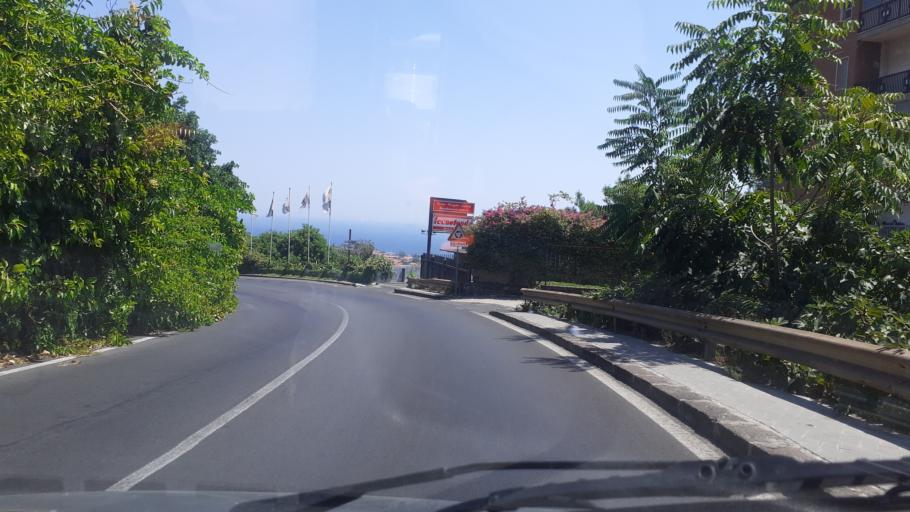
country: IT
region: Sicily
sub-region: Catania
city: Canalicchio
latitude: 37.5377
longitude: 15.0970
